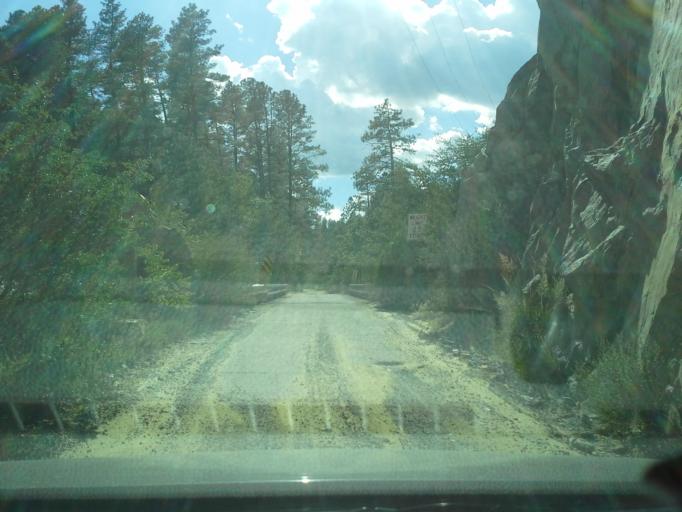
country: US
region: Arizona
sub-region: Yavapai County
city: Mayer
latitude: 34.2116
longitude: -112.3326
